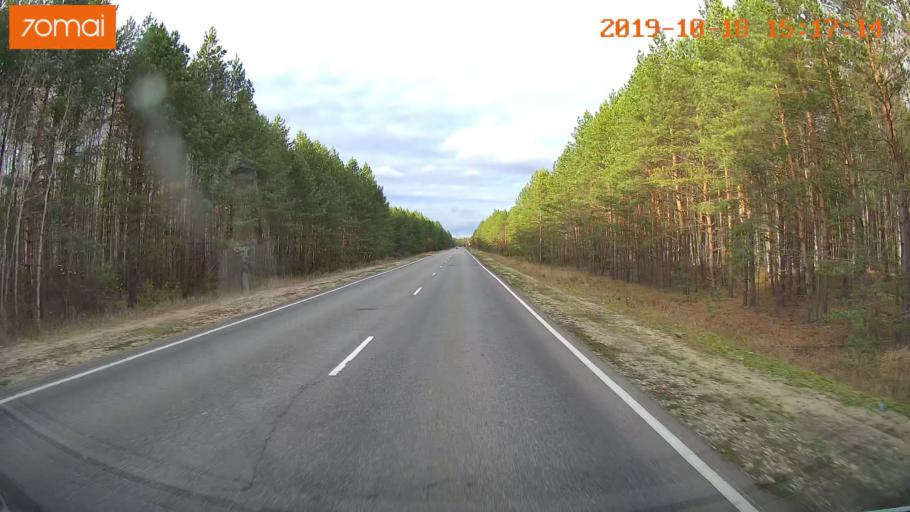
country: RU
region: Vladimir
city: Anopino
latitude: 55.6466
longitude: 40.7261
